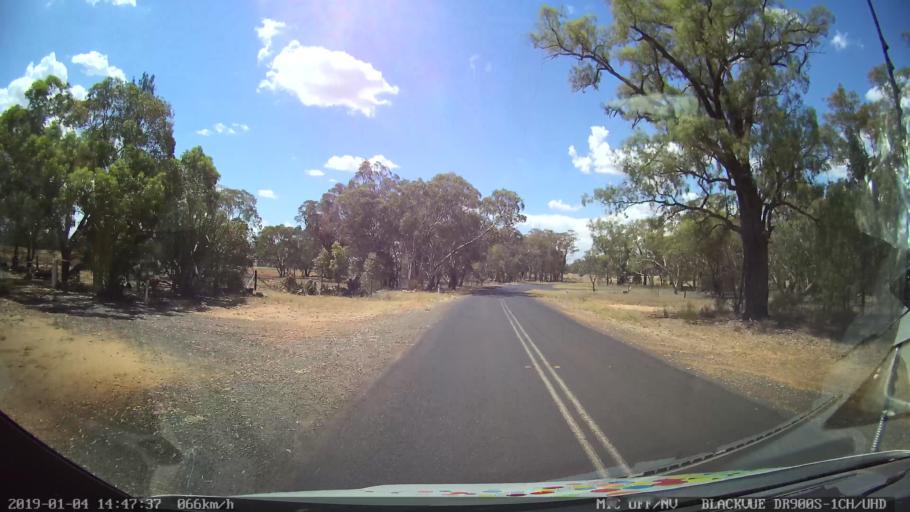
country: AU
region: New South Wales
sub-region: Dubbo Municipality
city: Dubbo
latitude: -32.0671
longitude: 148.6605
